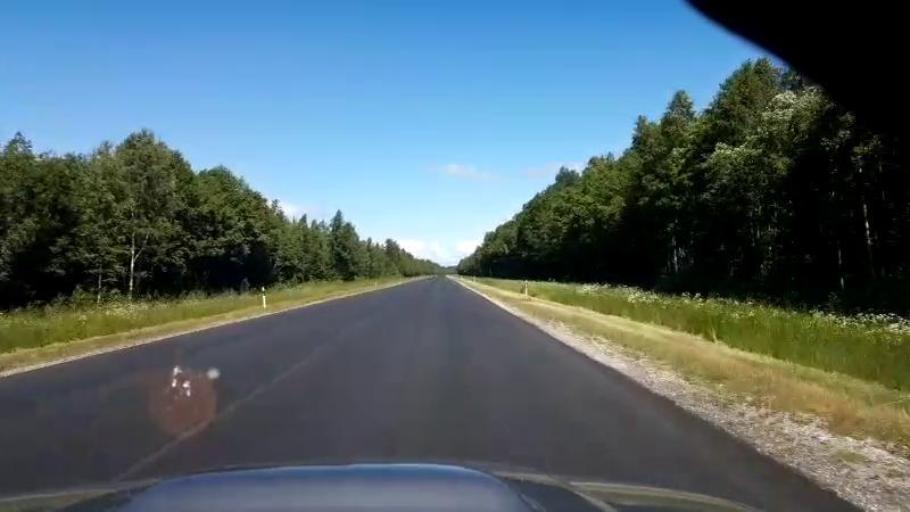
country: LV
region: Salacgrivas
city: Ainazi
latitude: 57.9285
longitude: 24.4258
